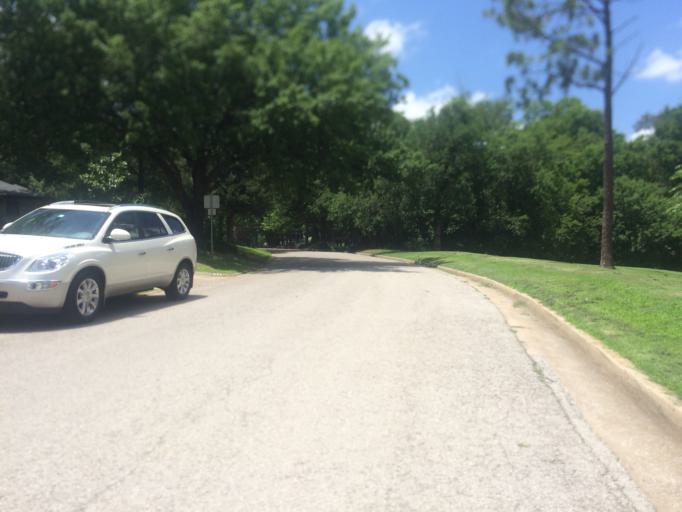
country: US
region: Oklahoma
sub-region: Cleveland County
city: Norman
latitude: 35.2122
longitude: -97.4327
